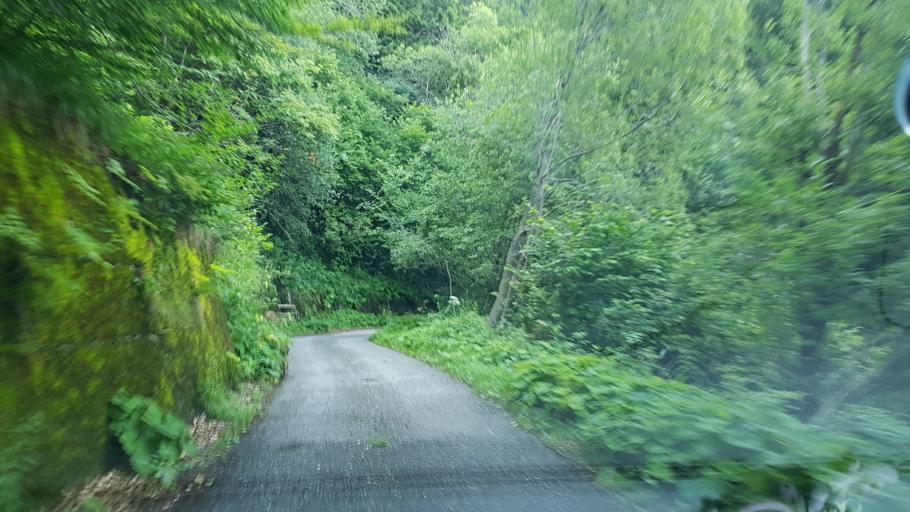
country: IT
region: Friuli Venezia Giulia
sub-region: Provincia di Udine
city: Cercivento
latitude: 46.5459
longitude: 12.9799
